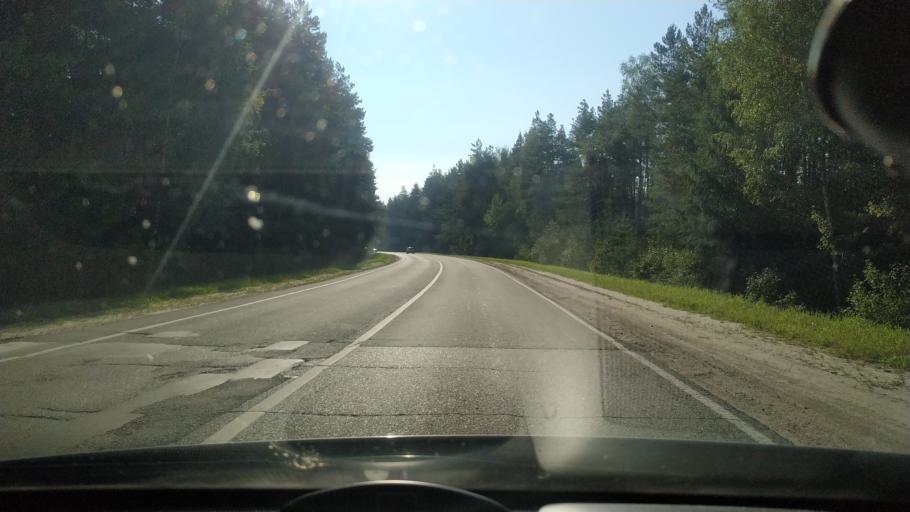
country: RU
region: Moskovskaya
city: Kerva
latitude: 55.5643
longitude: 39.6552
